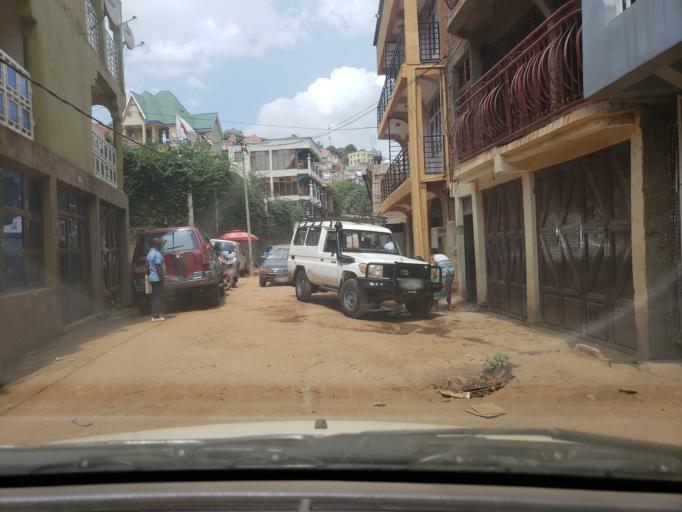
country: CD
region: South Kivu
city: Bukavu
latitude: -2.4969
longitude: 28.8584
